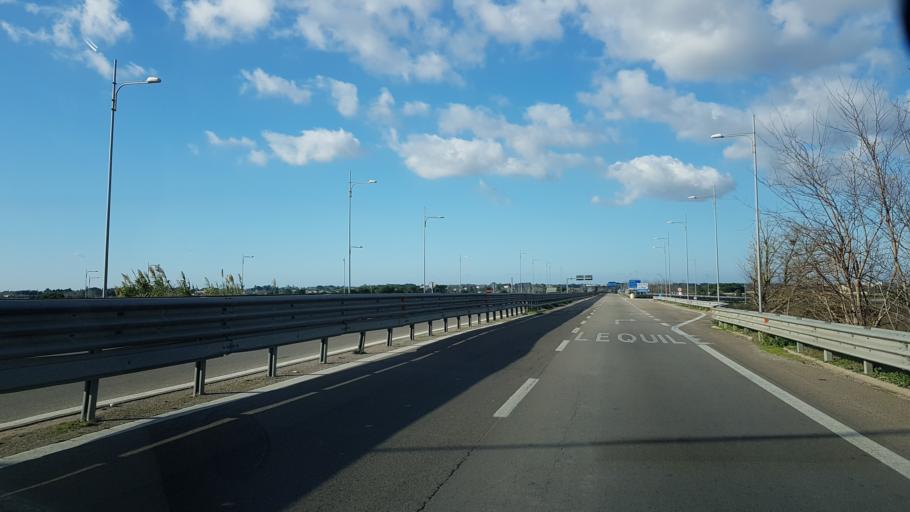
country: IT
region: Apulia
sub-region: Provincia di Lecce
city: Castromediano
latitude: 40.3262
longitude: 18.1565
